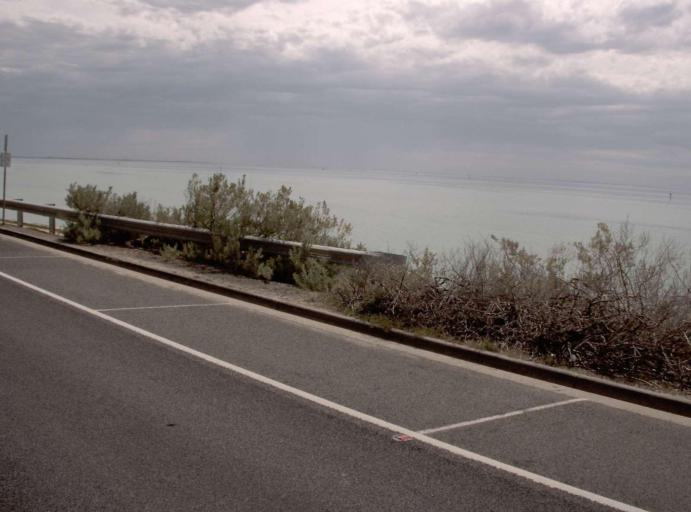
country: AU
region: Victoria
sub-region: Mornington Peninsula
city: McCrae
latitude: -38.3427
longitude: 144.9406
